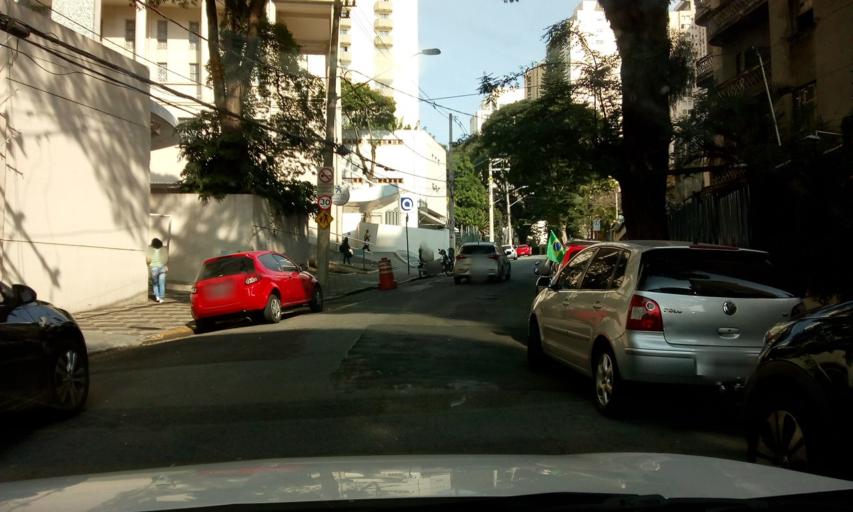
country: BR
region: Sao Paulo
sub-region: Sao Paulo
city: Sao Paulo
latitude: -23.5599
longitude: -46.6476
